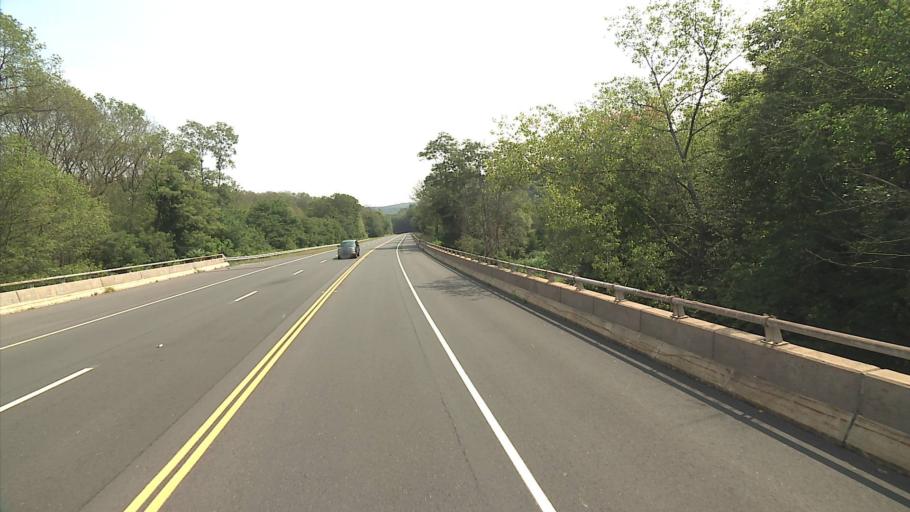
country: US
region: Connecticut
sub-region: Middlesex County
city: East Haddam
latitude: 41.4407
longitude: -72.4806
